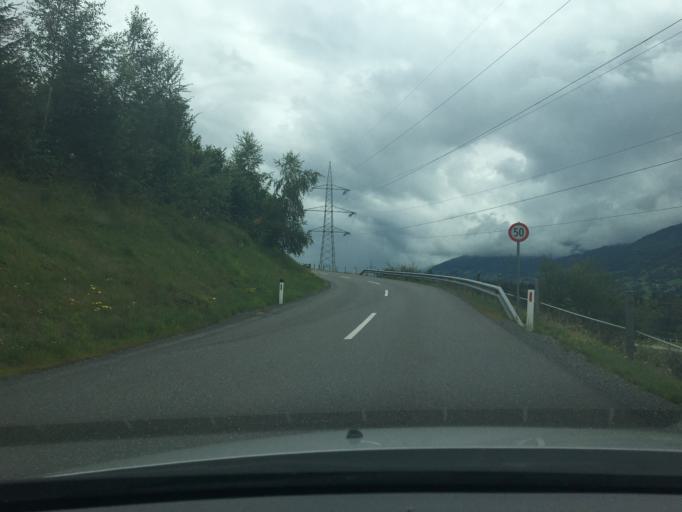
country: AT
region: Salzburg
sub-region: Politischer Bezirk Zell am See
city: Kaprun
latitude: 47.2779
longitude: 12.7782
